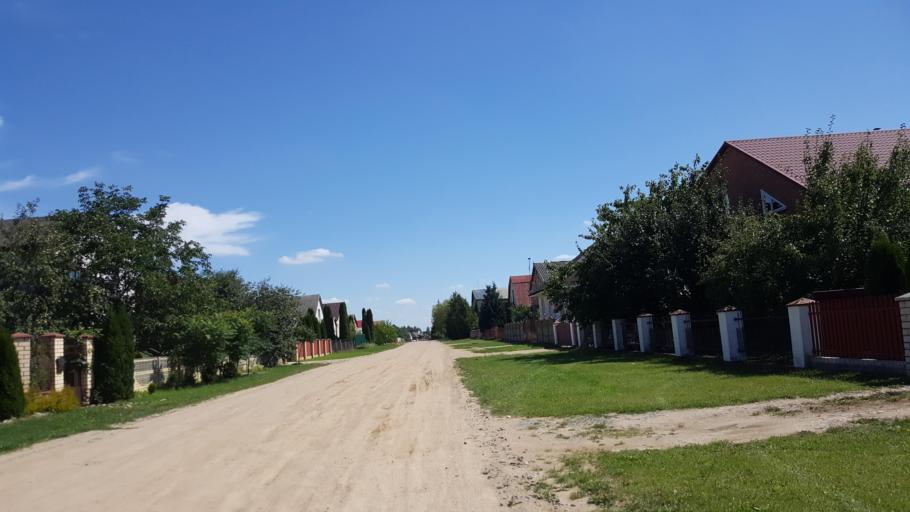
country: BY
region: Brest
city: Charnawchytsy
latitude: 52.2650
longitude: 23.5842
